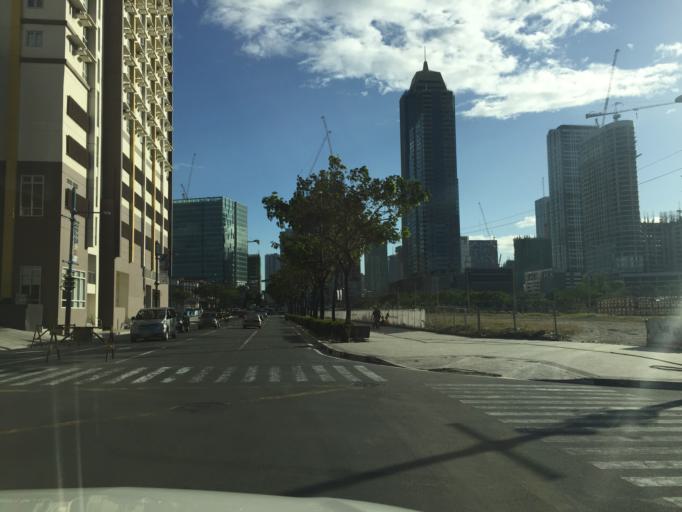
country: PH
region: Metro Manila
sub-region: Makati City
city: Makati City
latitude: 14.5608
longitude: 121.0547
